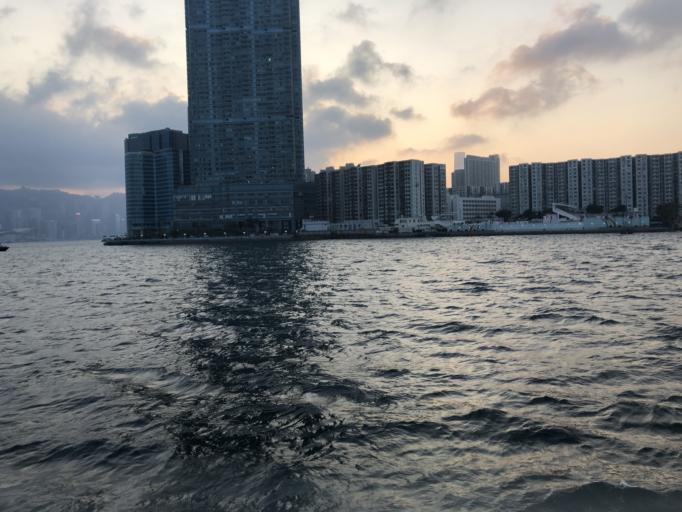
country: HK
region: Kowloon City
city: Kowloon
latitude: 22.3049
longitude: 114.1960
